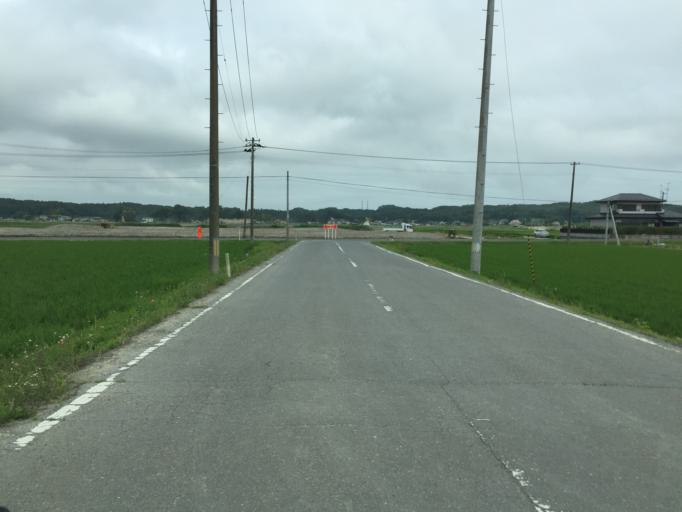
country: JP
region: Fukushima
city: Namie
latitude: 37.7293
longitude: 140.9822
